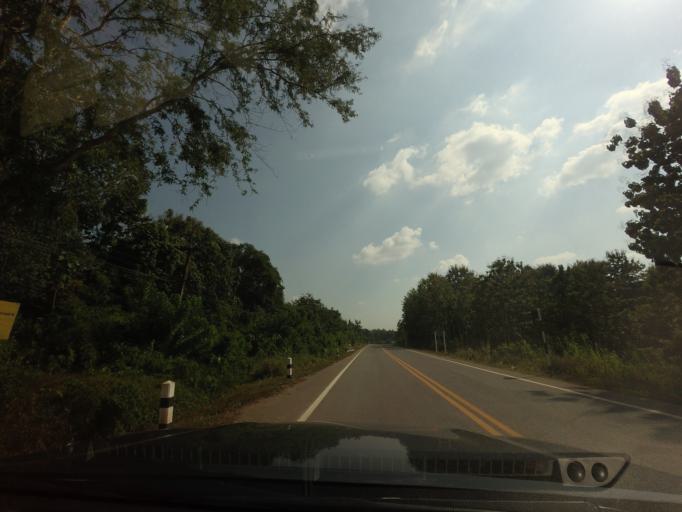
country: TH
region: Nan
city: Santi Suk
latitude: 18.9640
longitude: 100.9241
